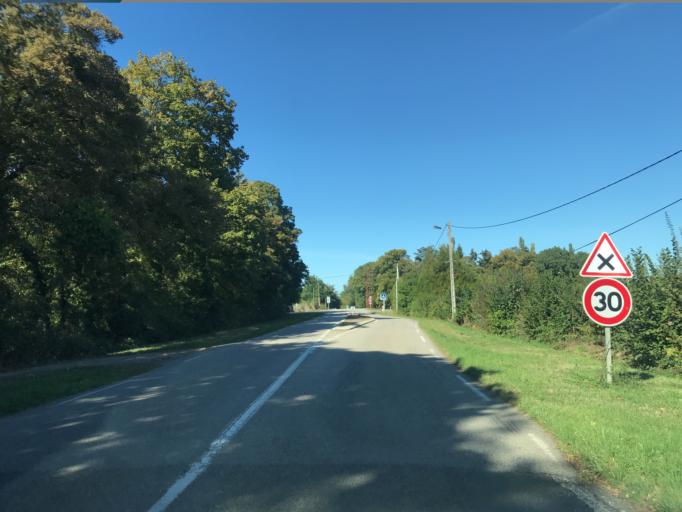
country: FR
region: Haute-Normandie
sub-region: Departement de l'Eure
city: Le Vaudreuil
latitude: 49.2427
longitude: 1.2108
